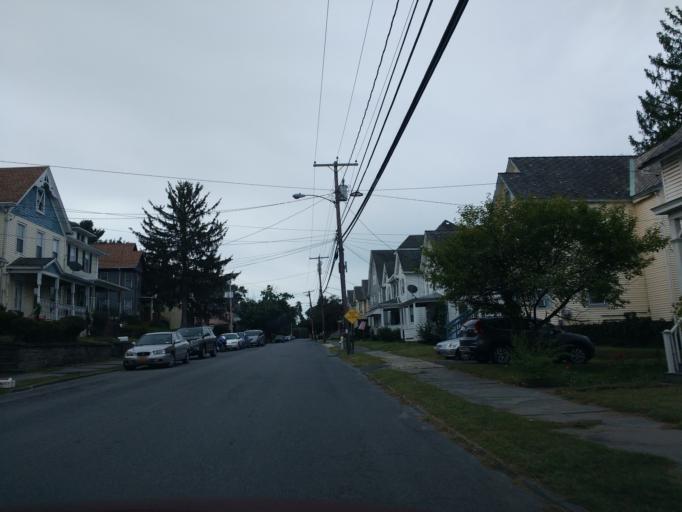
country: US
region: New York
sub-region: Ulster County
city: Kingston
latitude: 41.9263
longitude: -73.9986
